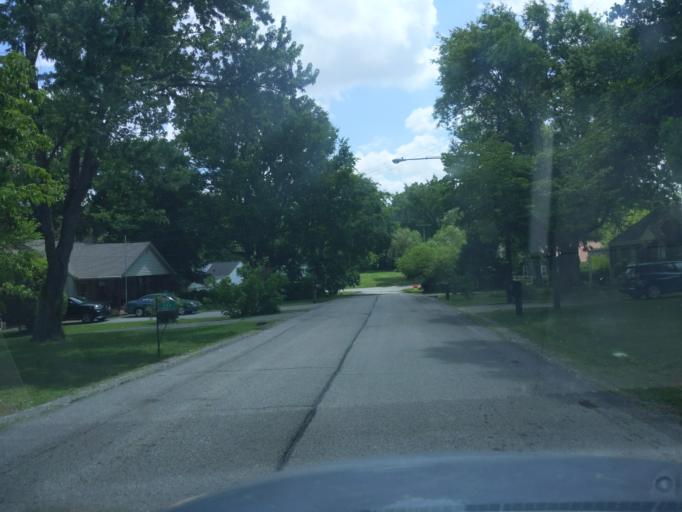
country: US
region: Tennessee
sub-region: Davidson County
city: Oak Hill
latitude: 36.1083
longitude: -86.7373
